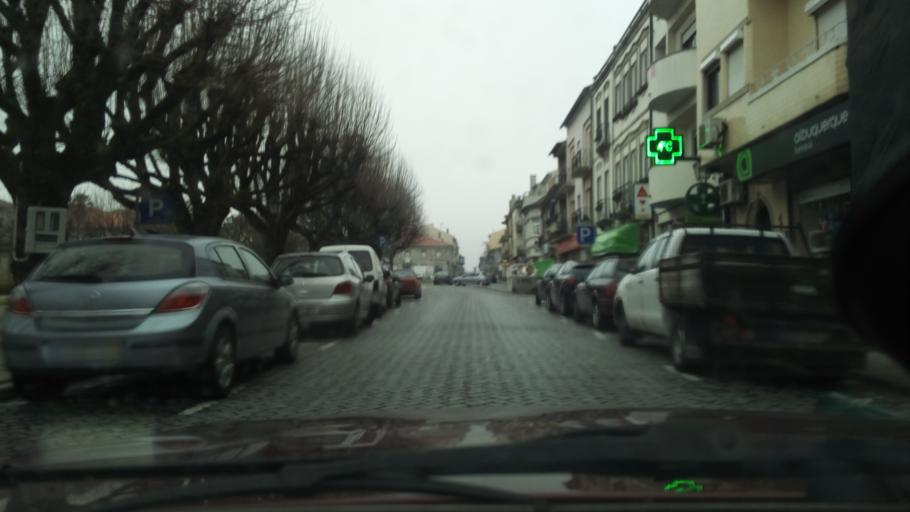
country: PT
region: Viseu
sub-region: Mangualde
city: Mangualde
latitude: 40.6046
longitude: -7.7588
